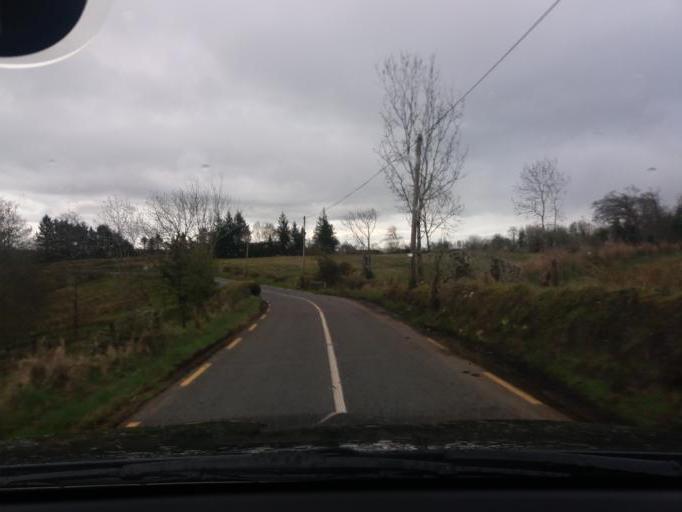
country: IE
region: Ulster
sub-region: An Cabhan
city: Ballyconnell
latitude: 54.1569
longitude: -7.7576
